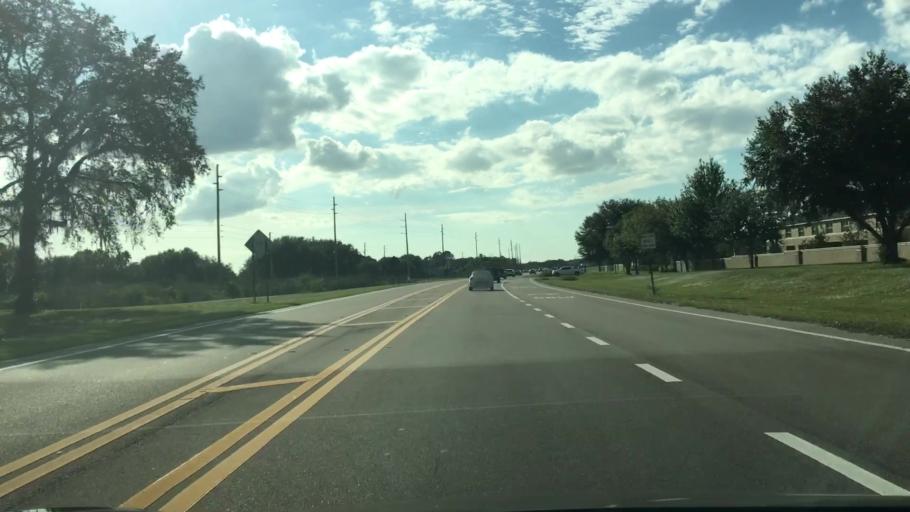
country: US
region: Florida
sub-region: Pasco County
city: Trinity
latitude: 28.1791
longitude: -82.6566
